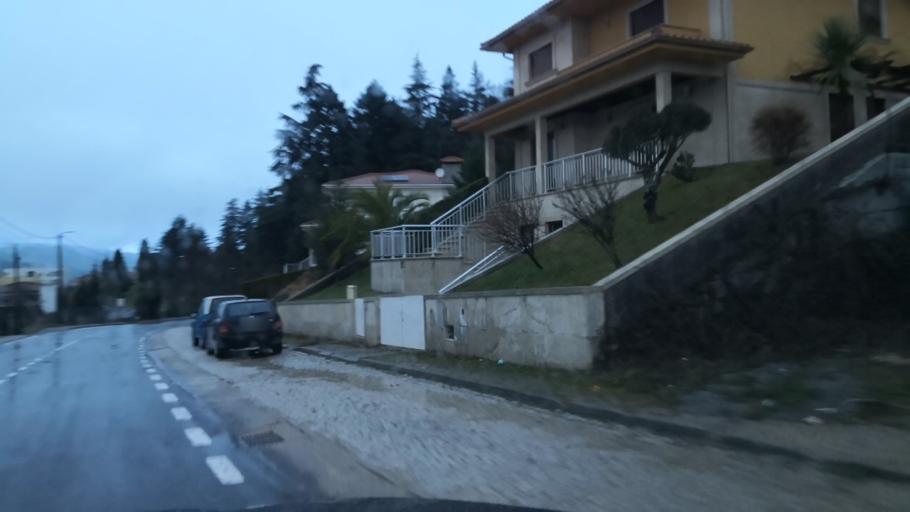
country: PT
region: Vila Real
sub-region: Vila Pouca de Aguiar
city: Vila Pouca de Aguiar
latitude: 41.4974
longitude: -7.6411
